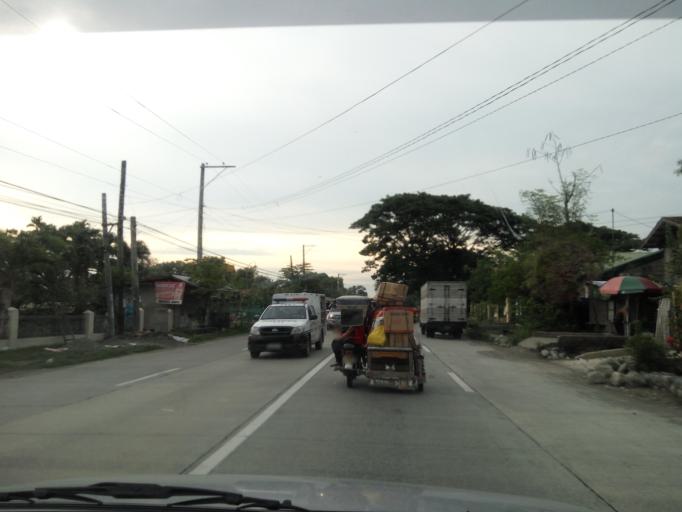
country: PH
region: Ilocos
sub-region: Province of Pangasinan
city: Bobonan
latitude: 16.1345
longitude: 120.5271
